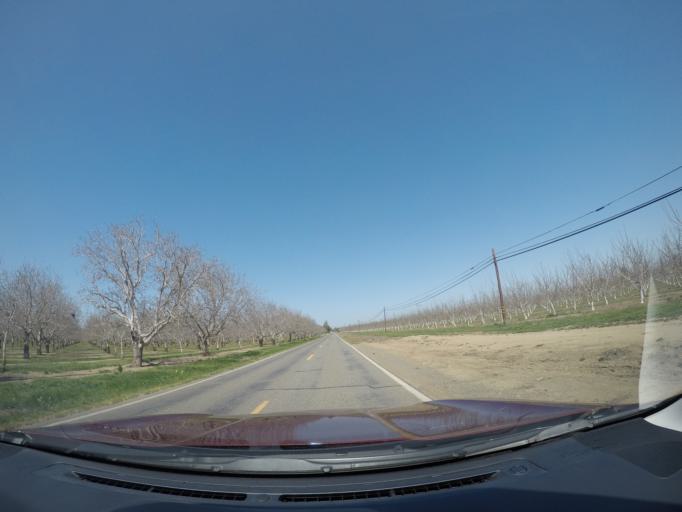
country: US
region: California
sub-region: Yolo County
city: Winters
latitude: 38.5049
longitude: -121.9596
